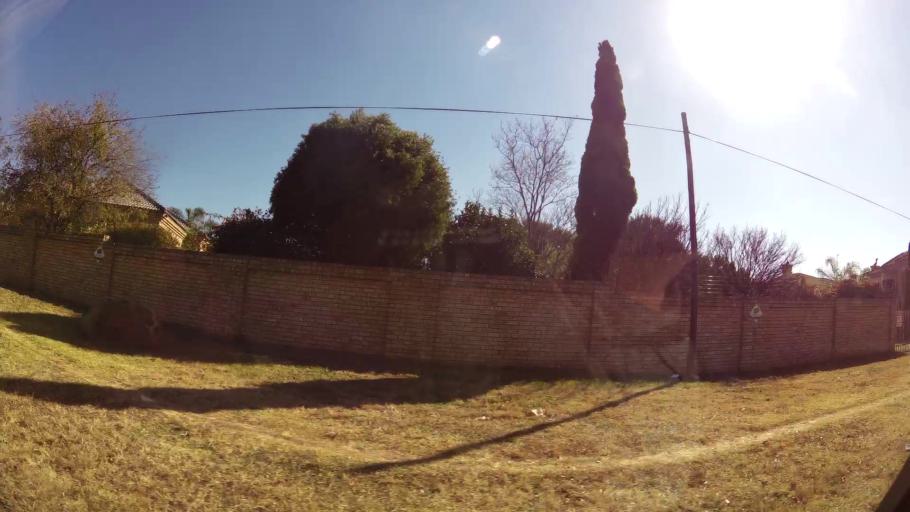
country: ZA
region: Gauteng
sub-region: Ekurhuleni Metropolitan Municipality
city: Germiston
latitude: -26.2971
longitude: 28.1015
